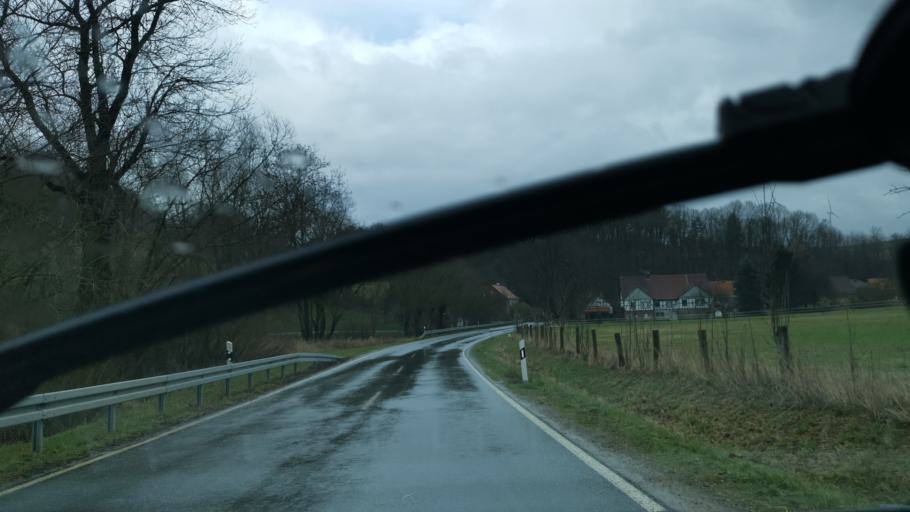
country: DE
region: Hesse
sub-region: Regierungsbezirk Kassel
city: Cornberg
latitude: 51.0620
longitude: 9.8844
